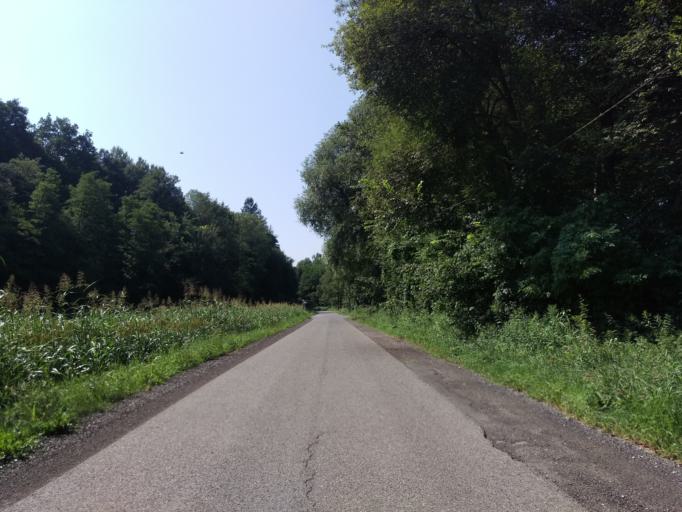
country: AT
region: Styria
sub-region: Politischer Bezirk Graz-Umgebung
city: Werndorf
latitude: 46.9074
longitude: 15.4937
